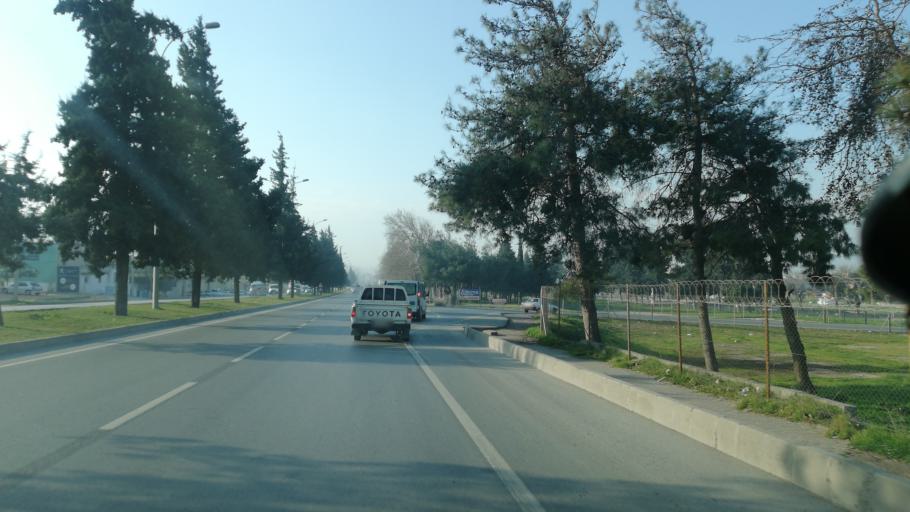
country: TR
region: Kahramanmaras
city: Kahramanmaras
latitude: 37.5643
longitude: 36.9239
